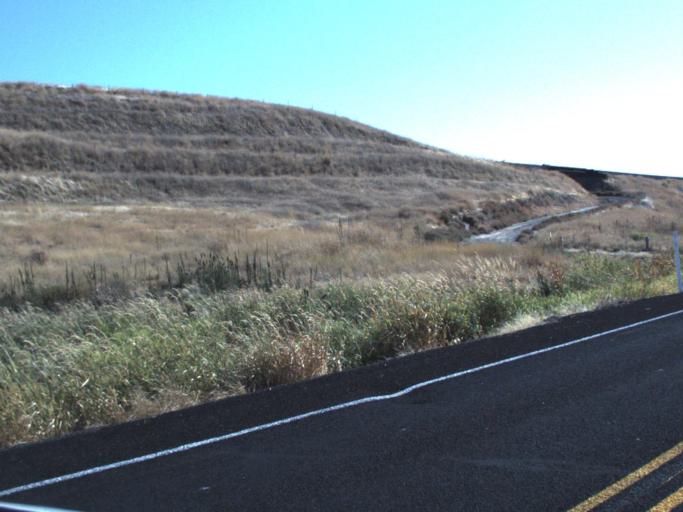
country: US
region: Washington
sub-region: Walla Walla County
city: Waitsburg
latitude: 46.2901
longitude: -118.3394
